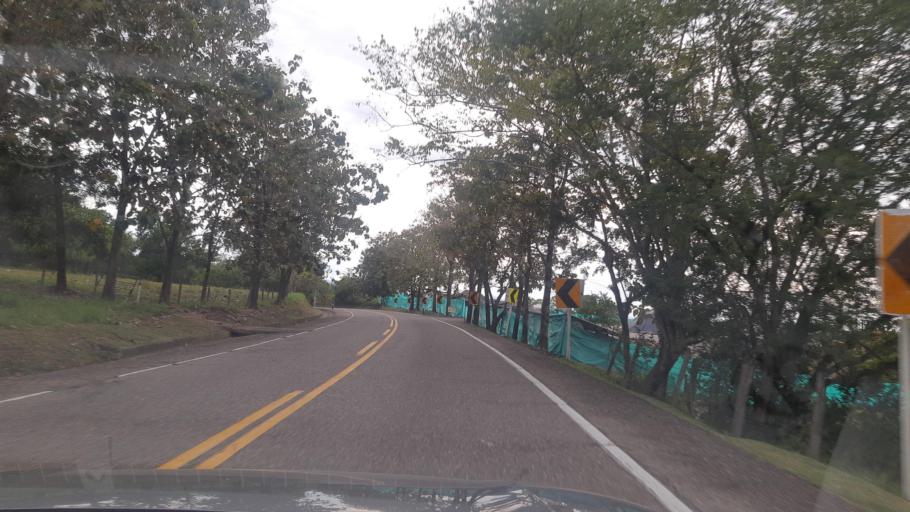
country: CO
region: Antioquia
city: Puerto Triunfo
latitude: 5.9004
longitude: -74.6336
